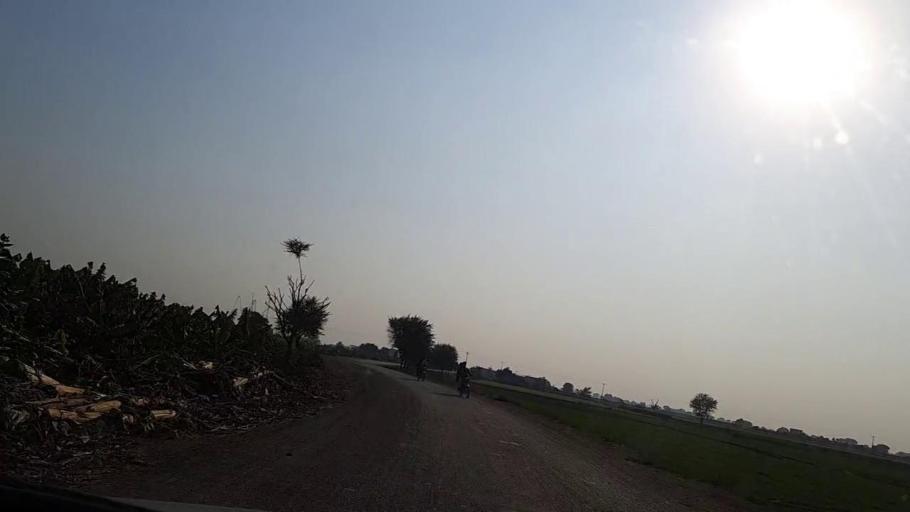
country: PK
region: Sindh
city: Sakrand
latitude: 26.0738
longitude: 68.2621
